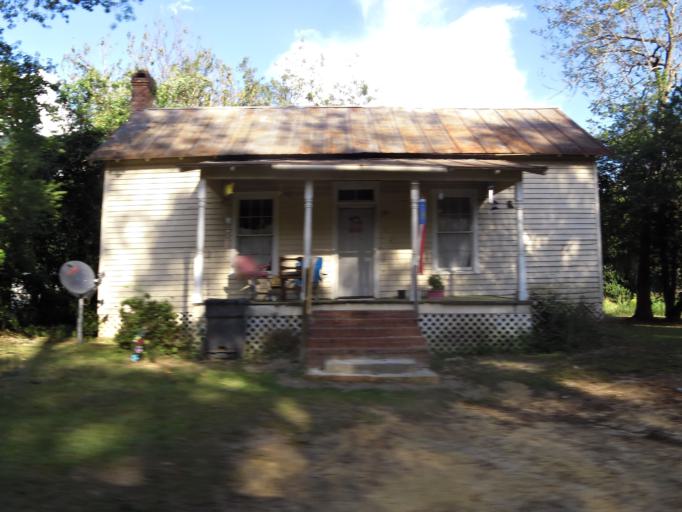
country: US
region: Georgia
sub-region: Brooks County
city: Quitman
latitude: 30.7818
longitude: -83.5528
